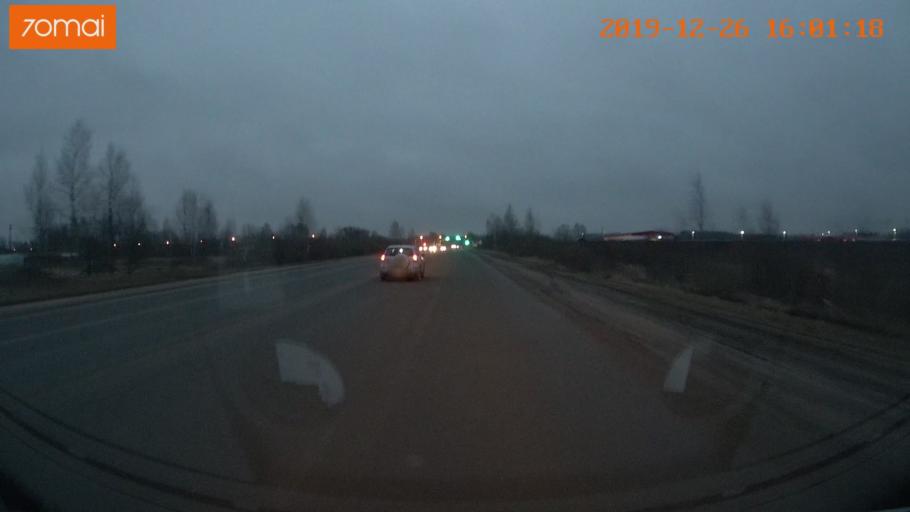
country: RU
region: Jaroslavl
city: Rybinsk
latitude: 58.0167
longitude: 38.8178
